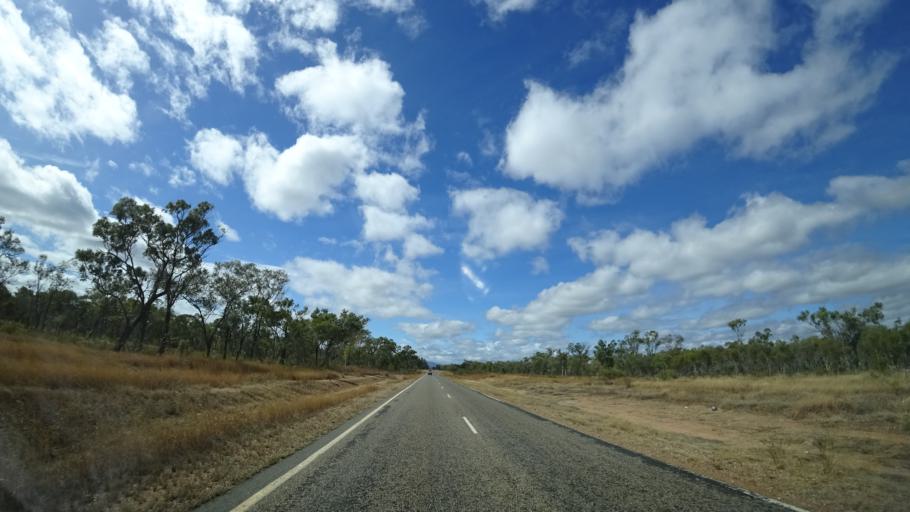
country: AU
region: Queensland
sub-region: Cairns
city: Port Douglas
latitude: -16.4922
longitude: 144.9426
